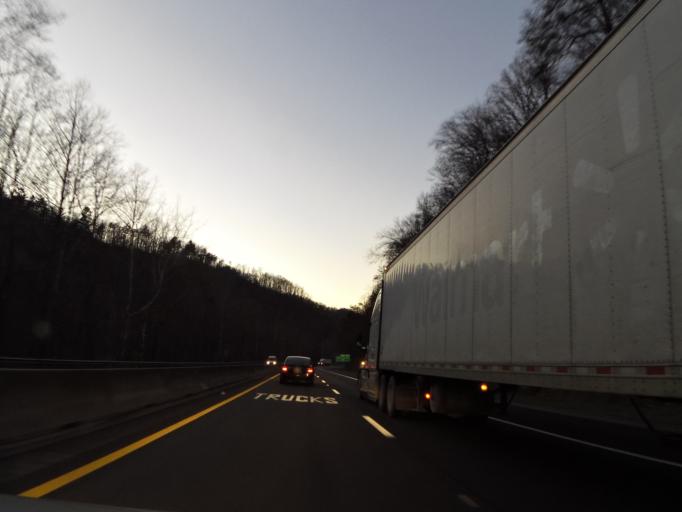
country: US
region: North Carolina
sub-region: Haywood County
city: Cove Creek
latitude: 35.7795
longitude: -83.1055
